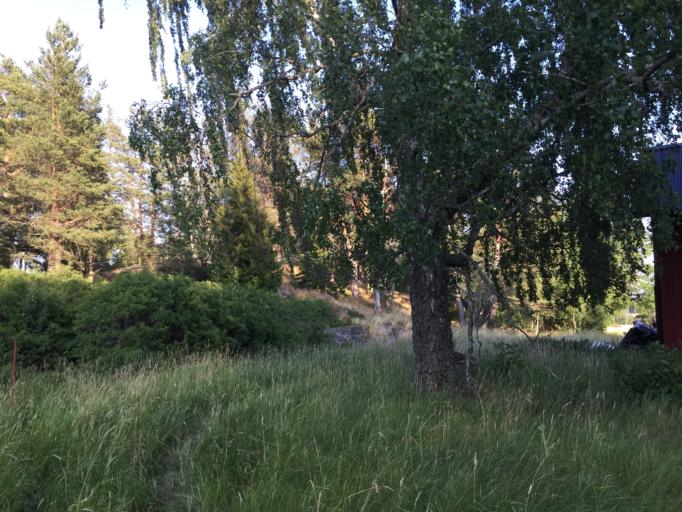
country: SE
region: Stockholm
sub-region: Salems Kommun
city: Ronninge
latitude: 59.2446
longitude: 17.6831
